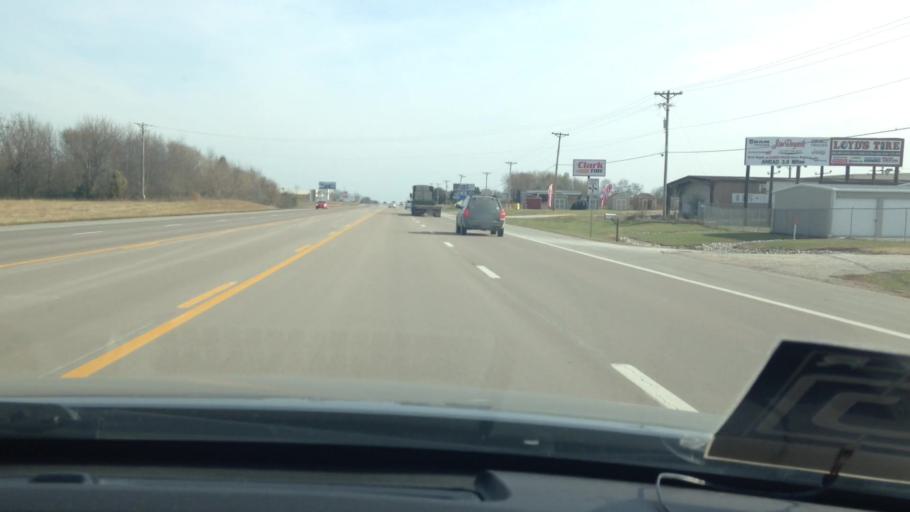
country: US
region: Missouri
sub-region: Henry County
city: Clinton
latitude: 38.3894
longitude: -93.8034
